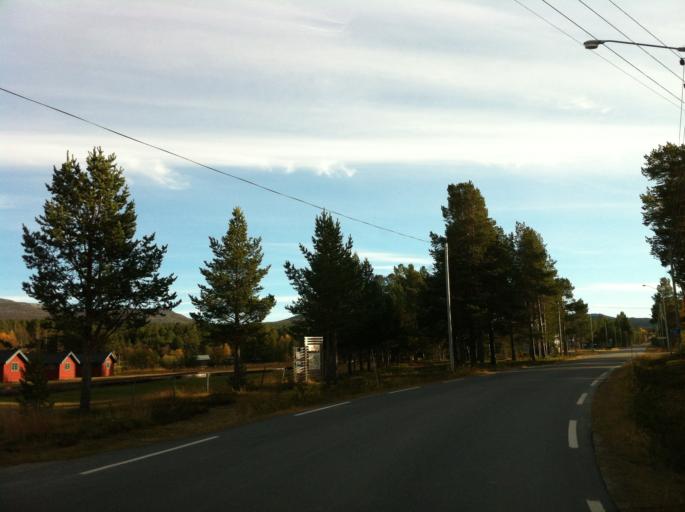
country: NO
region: Hedmark
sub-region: Engerdal
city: Engerdal
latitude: 62.1669
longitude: 11.9427
